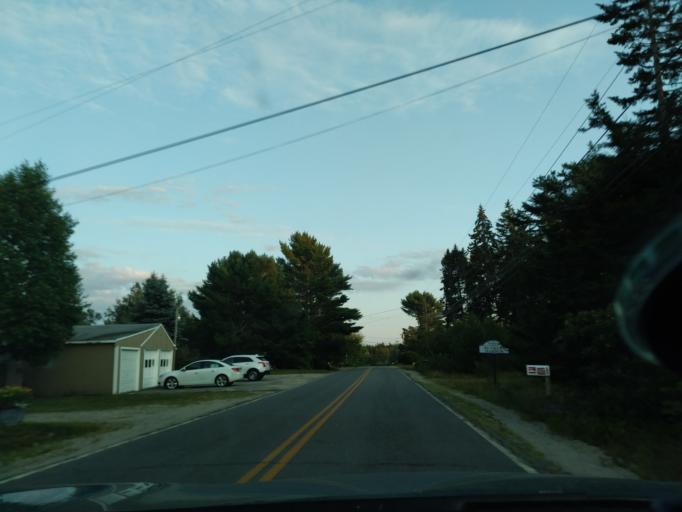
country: US
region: Maine
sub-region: Hancock County
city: Gouldsboro
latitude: 44.3759
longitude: -68.0355
